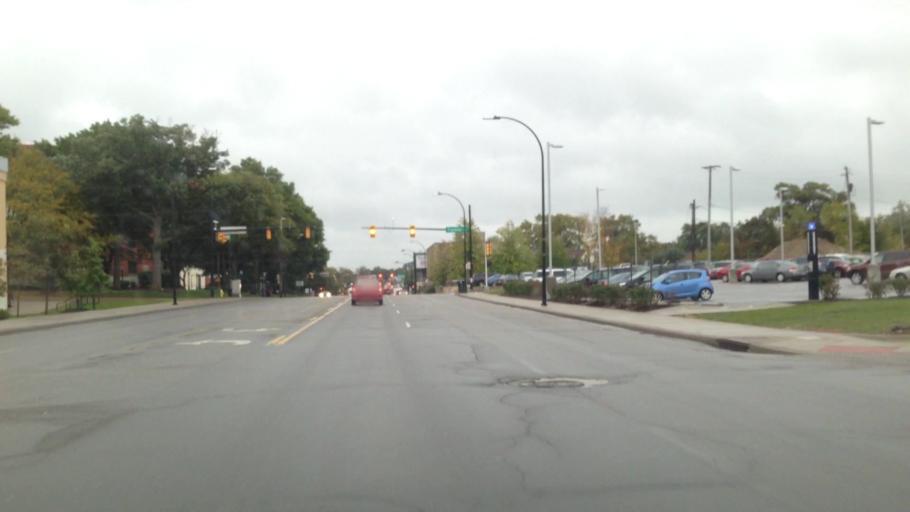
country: US
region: Ohio
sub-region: Summit County
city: Akron
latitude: 41.0793
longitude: -81.5025
